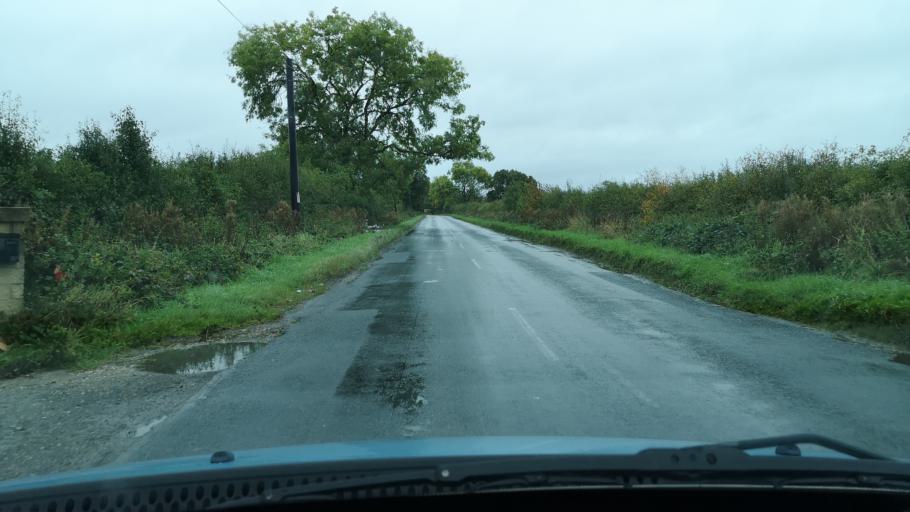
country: GB
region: England
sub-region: Doncaster
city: Moss
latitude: 53.6210
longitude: -1.0800
